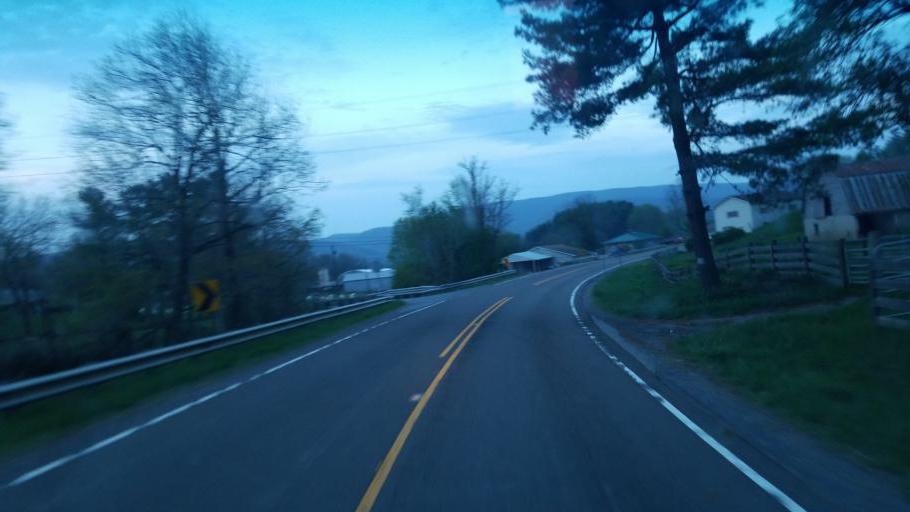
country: US
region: Virginia
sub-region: Smyth County
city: Atkins
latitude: 36.7929
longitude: -81.4007
